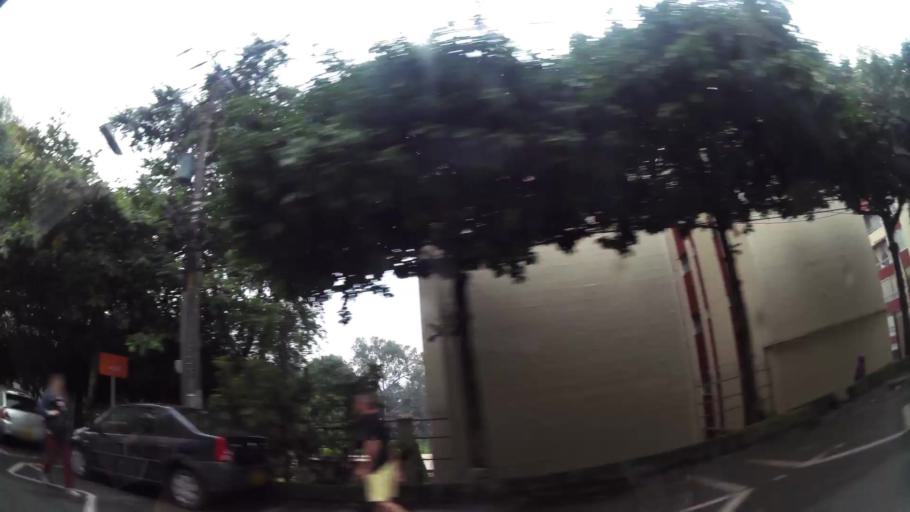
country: CO
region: Antioquia
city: Medellin
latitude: 6.2159
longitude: -75.5709
